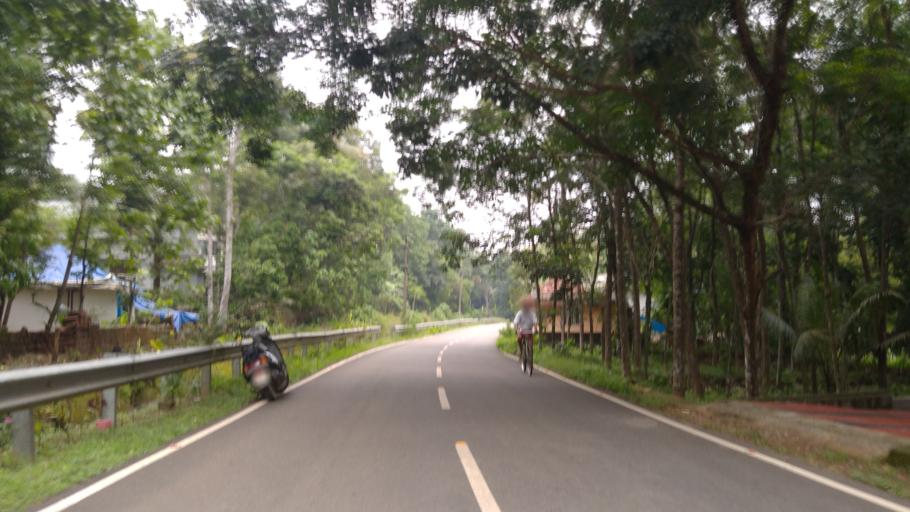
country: IN
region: Kerala
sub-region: Ernakulam
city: Ramamangalam
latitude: 10.0132
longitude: 76.4847
